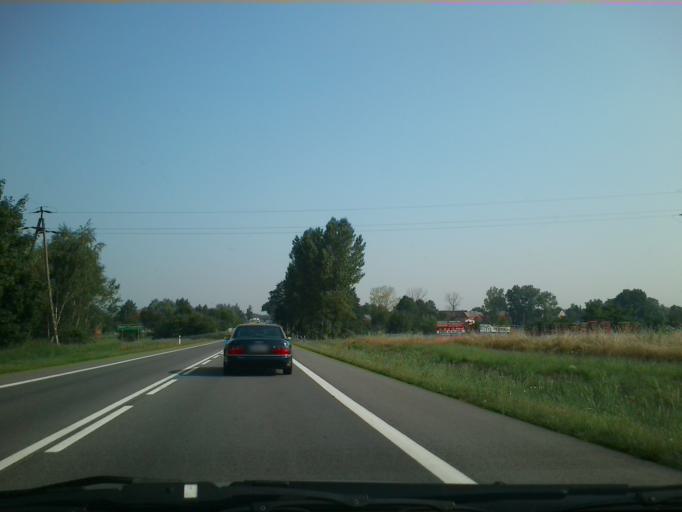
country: PL
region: Lubusz
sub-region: Powiat nowosolski
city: Nowe Miasteczko
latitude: 51.6985
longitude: 15.7291
